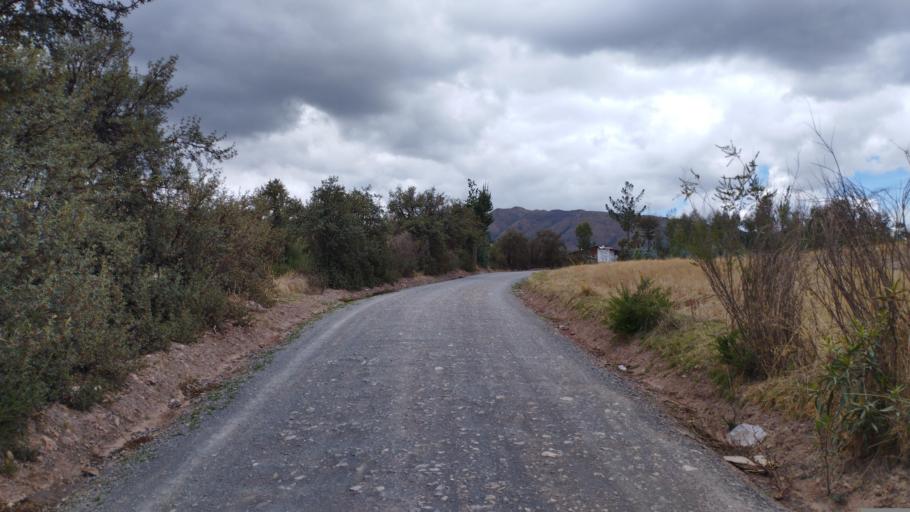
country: PE
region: Cusco
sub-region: Provincia de Cusco
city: Cusco
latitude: -13.5124
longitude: -71.9421
